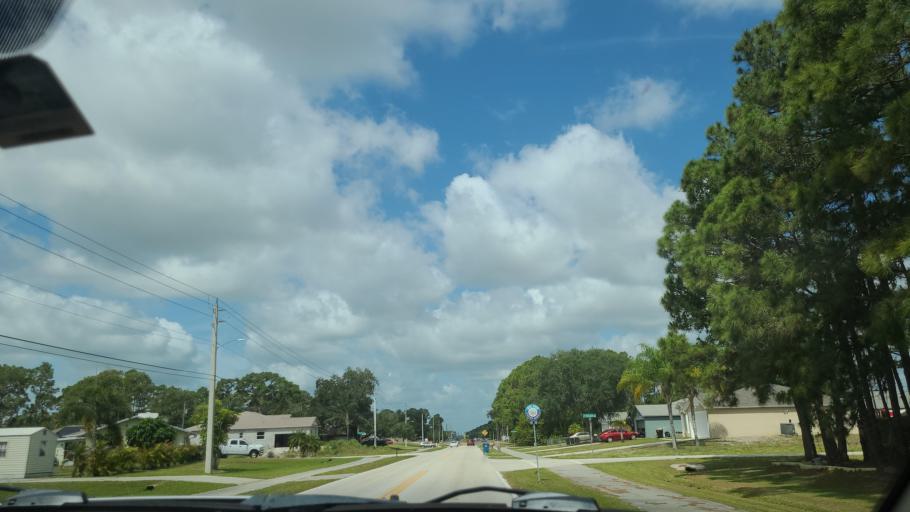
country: US
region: Florida
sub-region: Brevard County
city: West Melbourne
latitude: 27.9875
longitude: -80.6657
